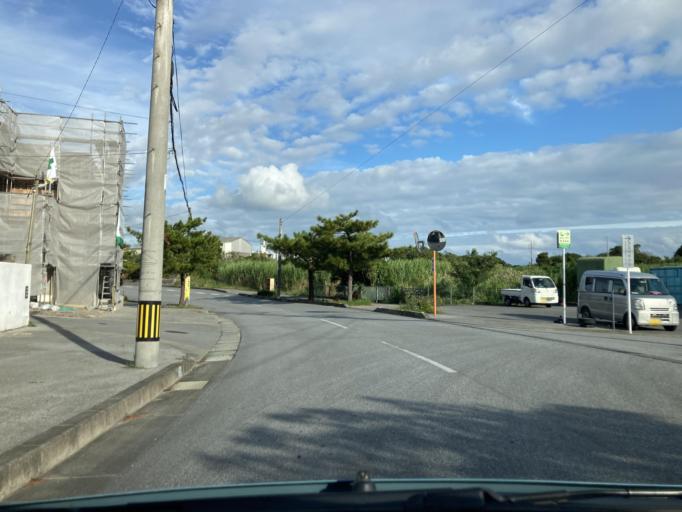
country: JP
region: Okinawa
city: Itoman
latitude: 26.1378
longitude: 127.7424
